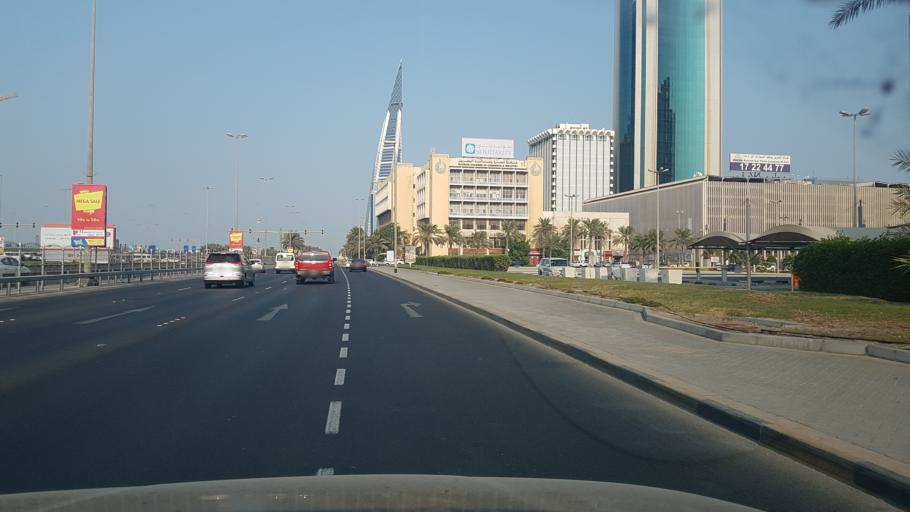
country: BH
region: Manama
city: Manama
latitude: 26.2357
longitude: 50.5740
